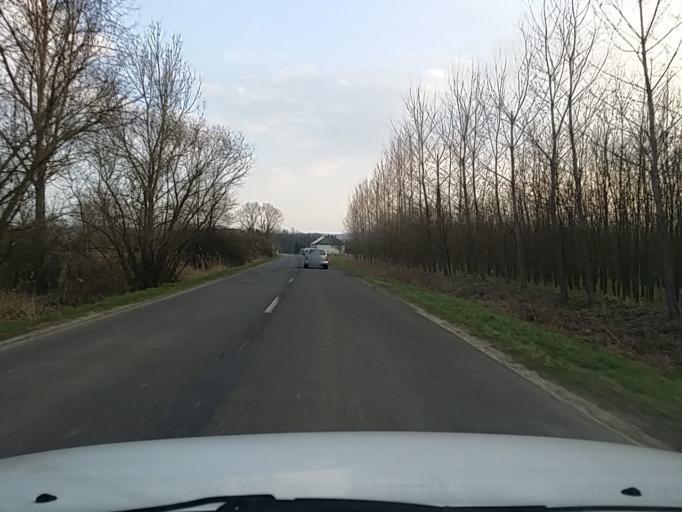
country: HU
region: Heves
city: Petervasara
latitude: 48.0243
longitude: 20.1095
